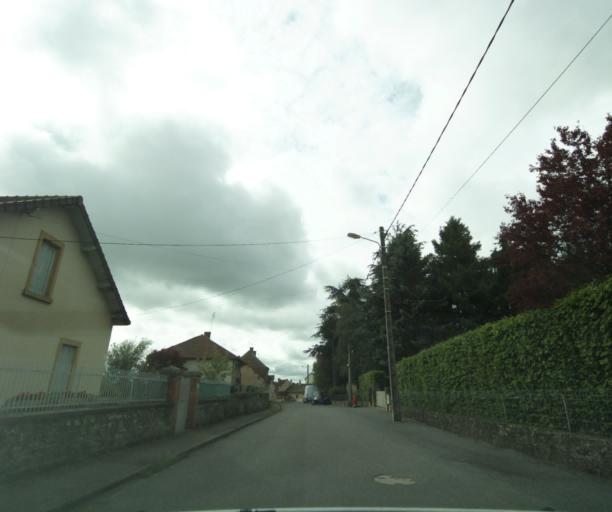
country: FR
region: Bourgogne
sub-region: Departement de Saone-et-Loire
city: Charolles
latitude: 46.4310
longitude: 4.2805
